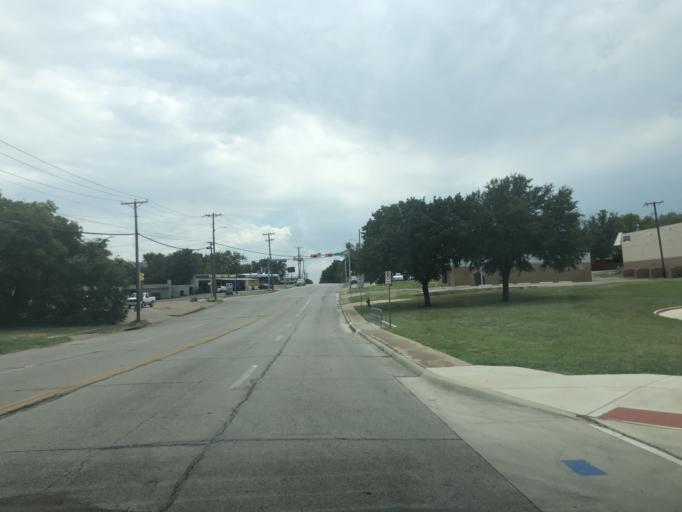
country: US
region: Texas
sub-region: Dallas County
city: Grand Prairie
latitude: 32.7369
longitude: -97.0058
